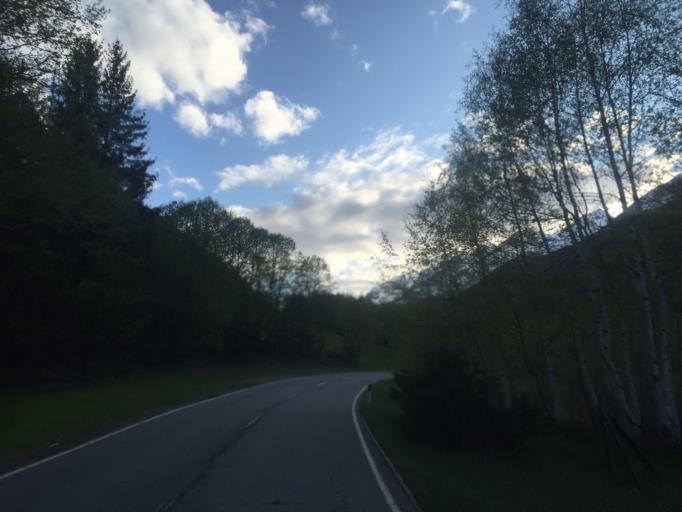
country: CH
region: Ticino
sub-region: Leventina District
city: Airolo
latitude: 46.5199
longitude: 8.5678
